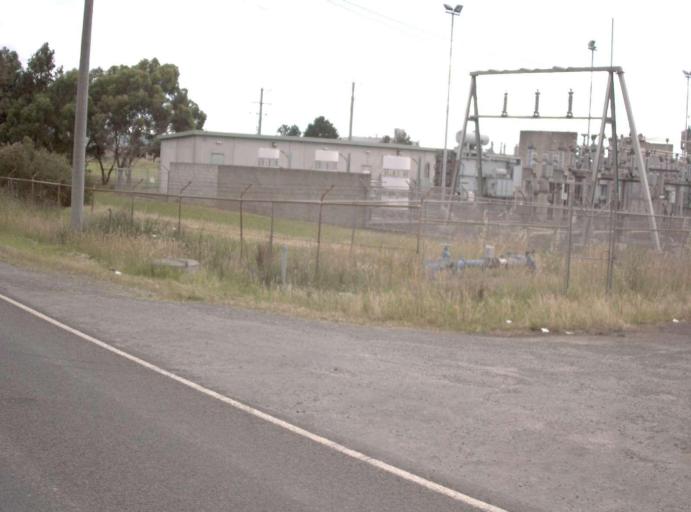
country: AU
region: Victoria
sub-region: Latrobe
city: Morwell
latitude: -38.1827
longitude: 146.4406
